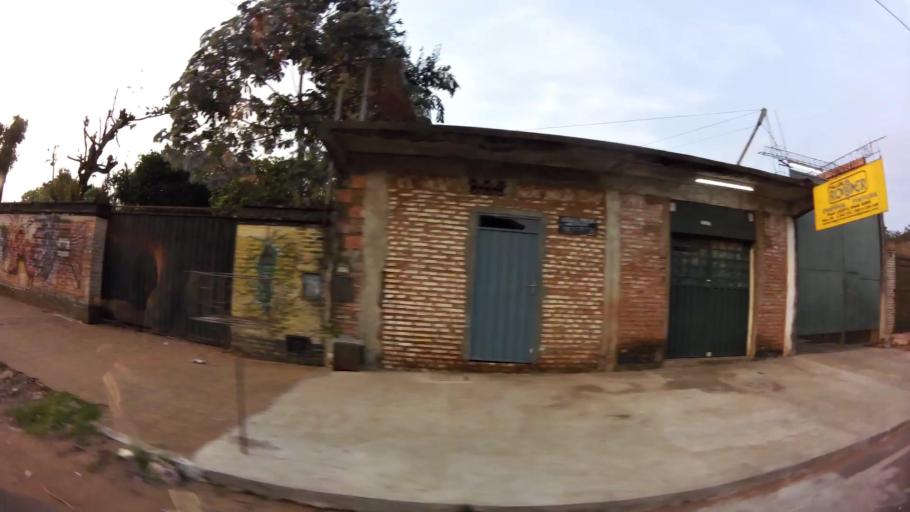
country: PY
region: Central
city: Lambare
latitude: -25.3575
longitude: -57.6069
